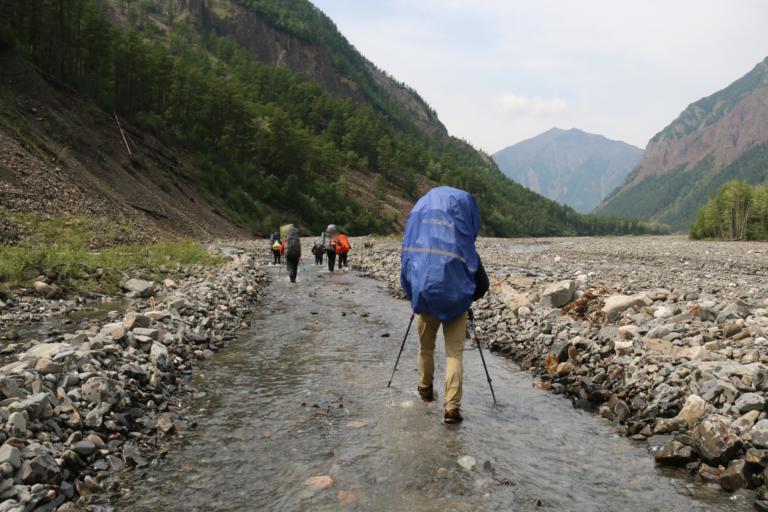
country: RU
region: Respublika Buryatiya
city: Novyy Uoyan
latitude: 56.2757
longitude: 111.4259
